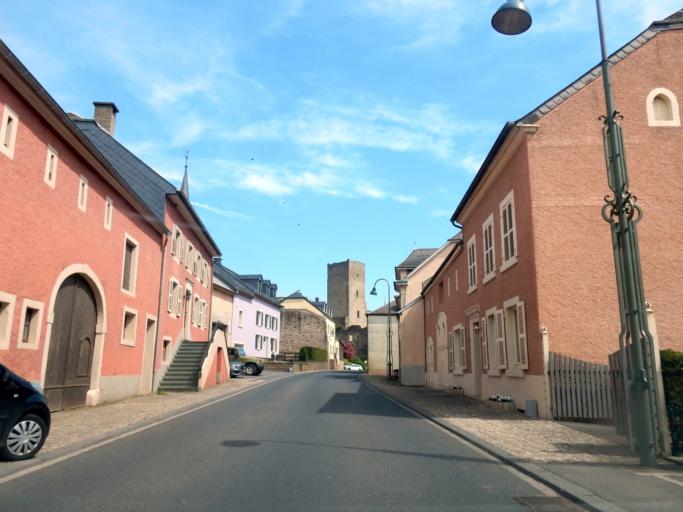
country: LU
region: Diekirch
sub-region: Canton de Redange
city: Useldange
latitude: 49.7667
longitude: 5.9797
